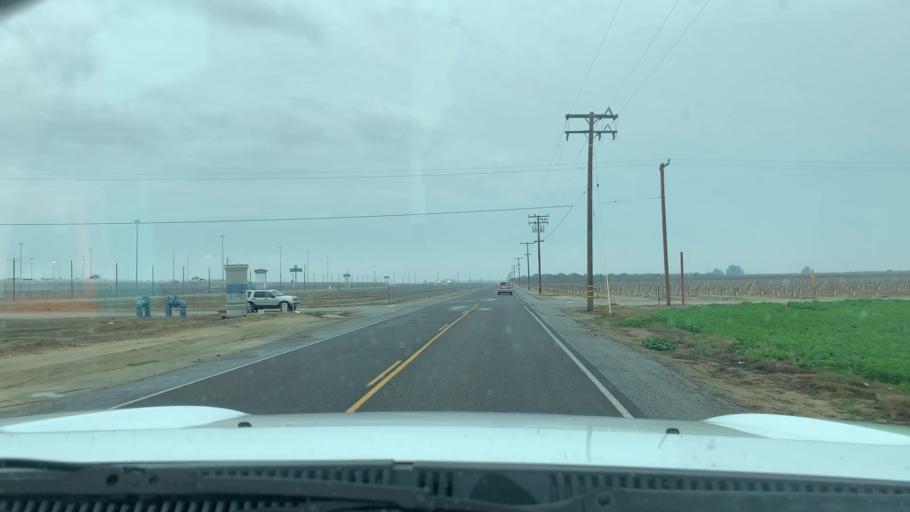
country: US
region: California
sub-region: Kern County
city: Delano
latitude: 35.7612
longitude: -119.3304
